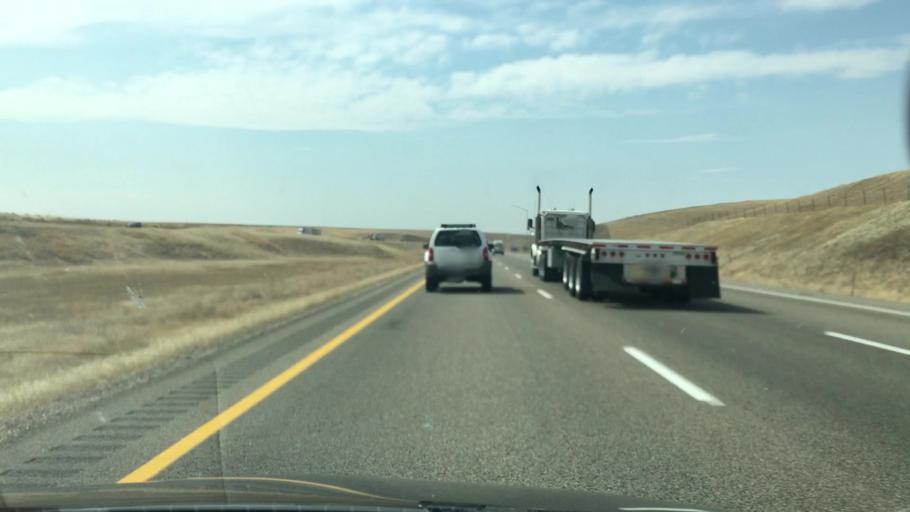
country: US
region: Idaho
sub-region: Ada County
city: Boise
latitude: 43.4844
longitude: -116.1150
